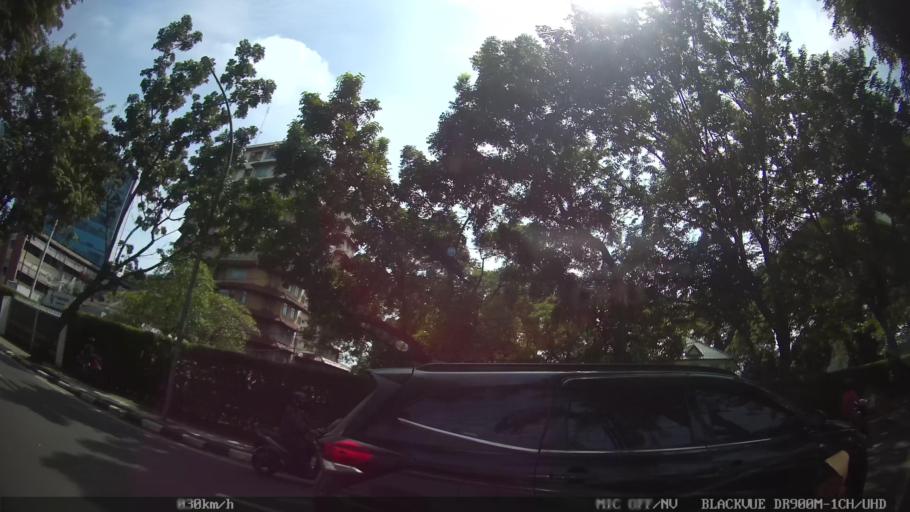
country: ID
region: North Sumatra
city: Medan
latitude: 3.5856
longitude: 98.6742
